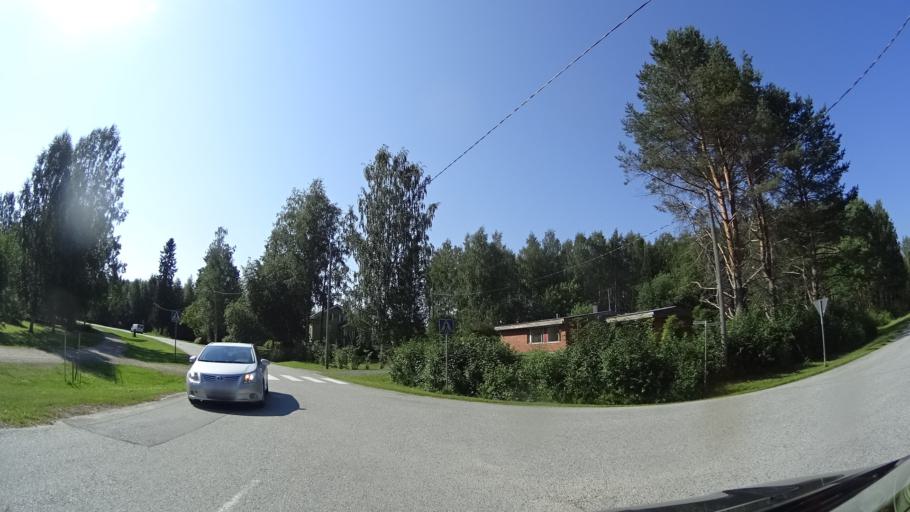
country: FI
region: North Karelia
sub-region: Joensuu
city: Juuka
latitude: 63.2366
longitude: 29.2449
